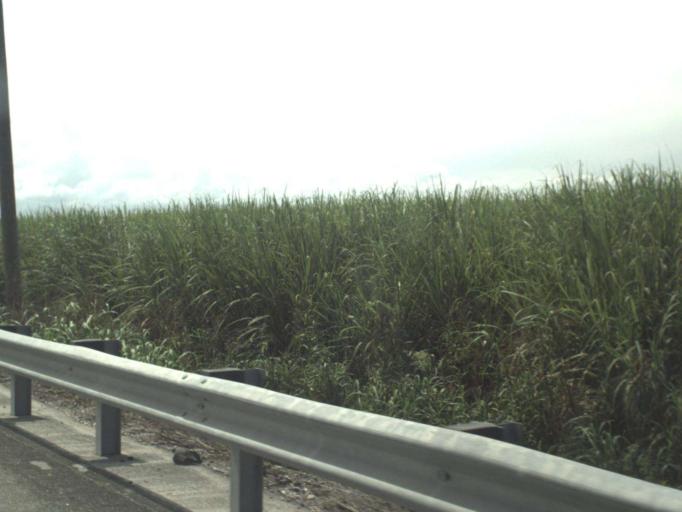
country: US
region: Florida
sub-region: Palm Beach County
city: Pahokee
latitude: 26.7897
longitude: -80.6534
